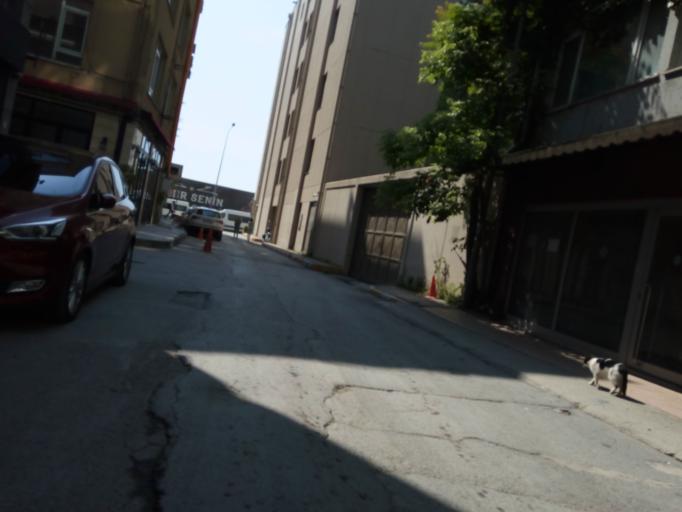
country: TR
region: Istanbul
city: Eminoenue
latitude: 41.0256
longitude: 28.9812
